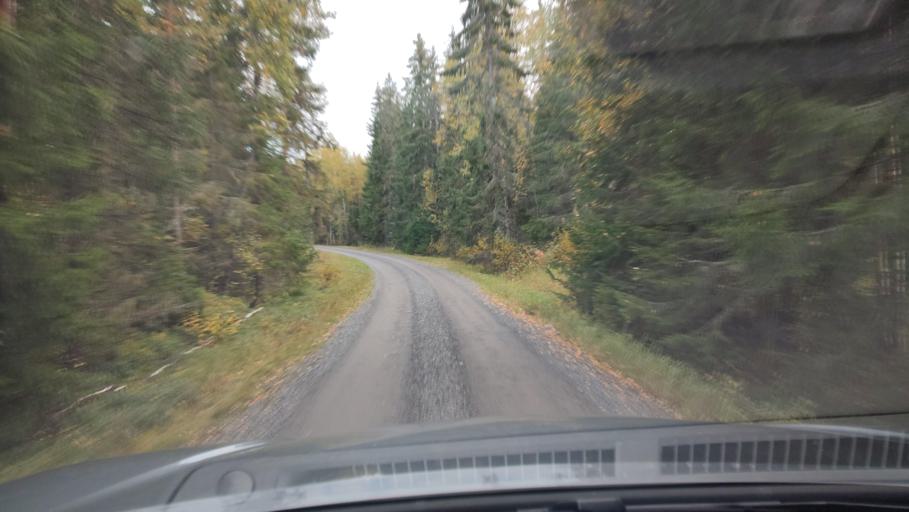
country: FI
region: Ostrobothnia
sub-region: Sydosterbotten
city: Kristinestad
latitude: 62.2330
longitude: 21.4017
